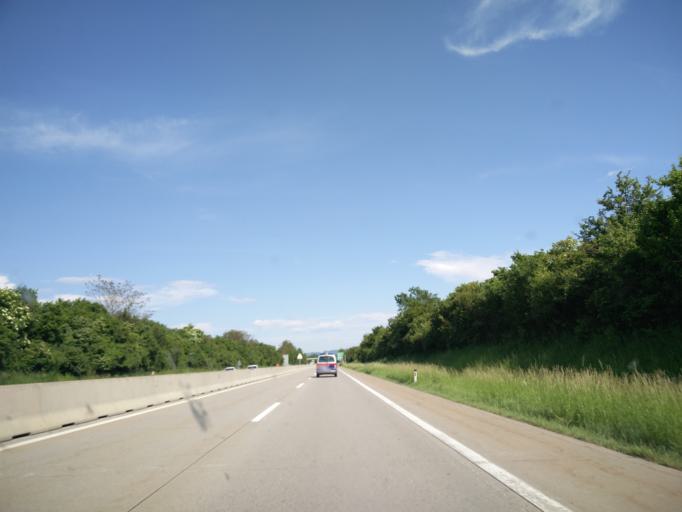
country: AT
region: Carinthia
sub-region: Politischer Bezirk Klagenfurt Land
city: Maria Saal
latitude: 46.6441
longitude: 14.3448
